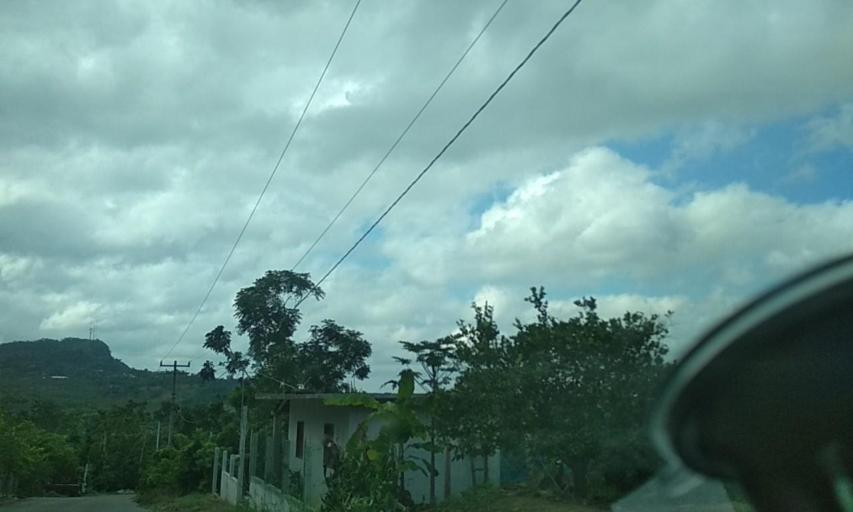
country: MX
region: Veracruz
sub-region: Papantla
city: Polutla
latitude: 20.5414
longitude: -97.2465
